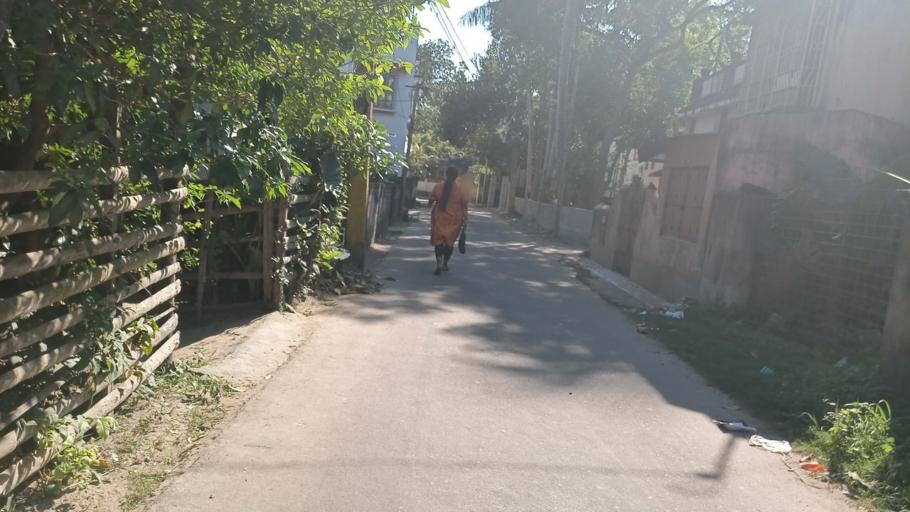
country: IN
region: West Bengal
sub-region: North 24 Parganas
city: Bangaon
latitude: 23.0523
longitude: 88.8242
